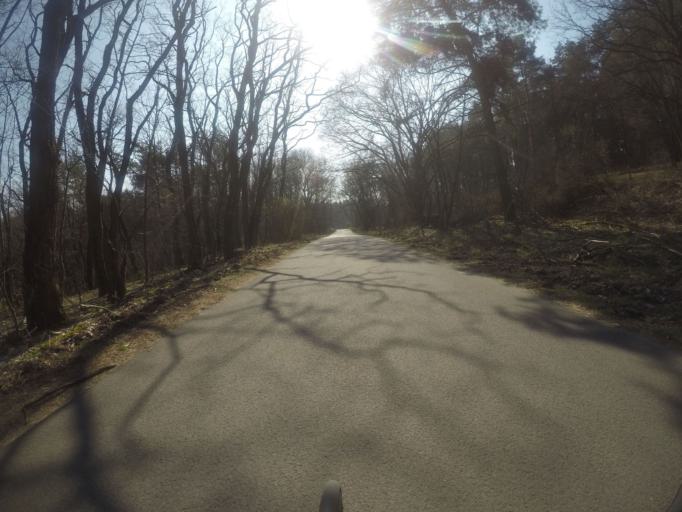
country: DE
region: Berlin
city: Muggelheim
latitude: 52.3828
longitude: 13.6987
